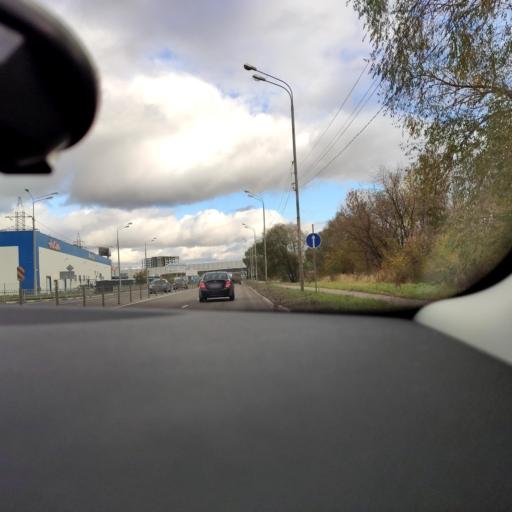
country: RU
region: Moskovskaya
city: Kotel'niki
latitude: 55.6513
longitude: 37.8500
